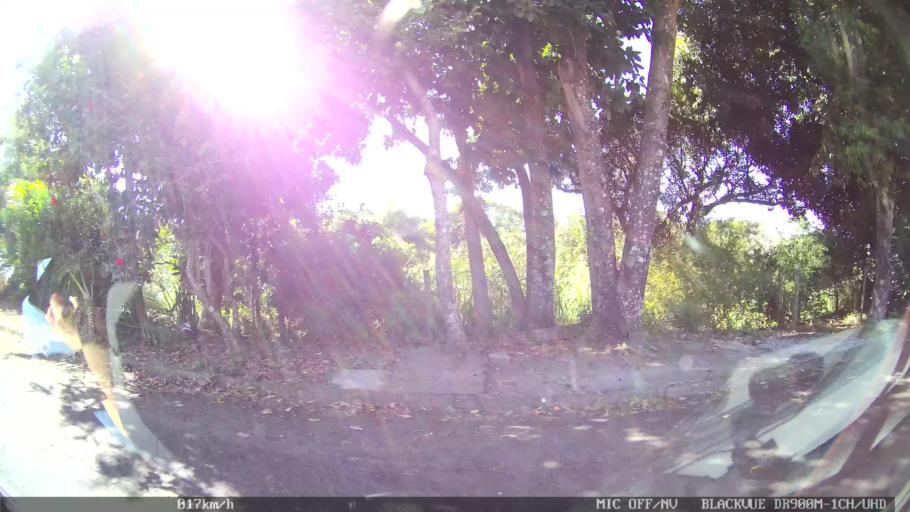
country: BR
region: Sao Paulo
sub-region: Franca
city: Franca
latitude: -20.5468
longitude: -47.3798
